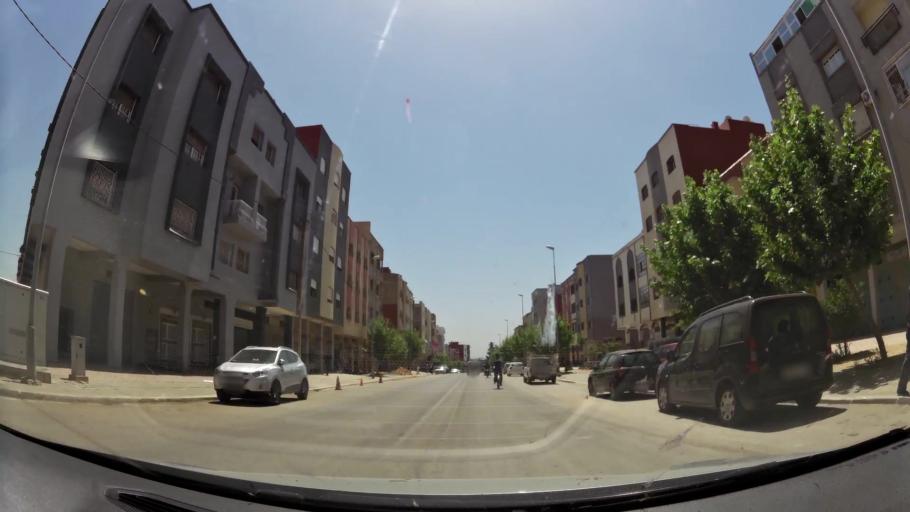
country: MA
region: Rabat-Sale-Zemmour-Zaer
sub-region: Khemisset
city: Khemisset
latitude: 33.8313
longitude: -6.0632
